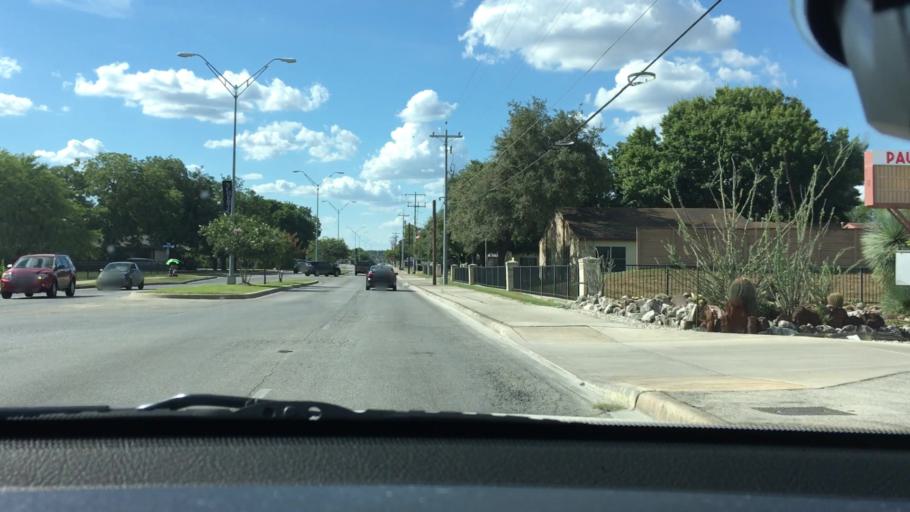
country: US
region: Texas
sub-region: Guadalupe County
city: Schertz
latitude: 29.5560
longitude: -98.2641
